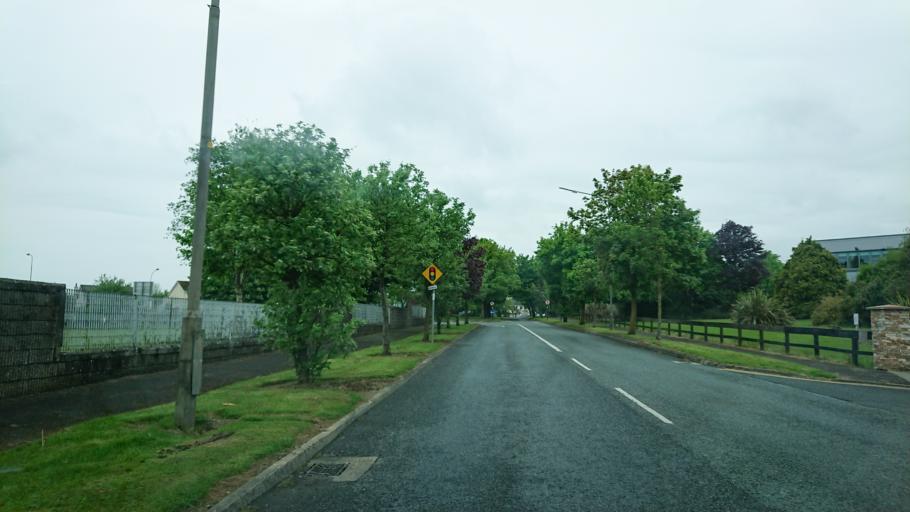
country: IE
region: Munster
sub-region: Waterford
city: Waterford
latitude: 52.2454
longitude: -7.1442
